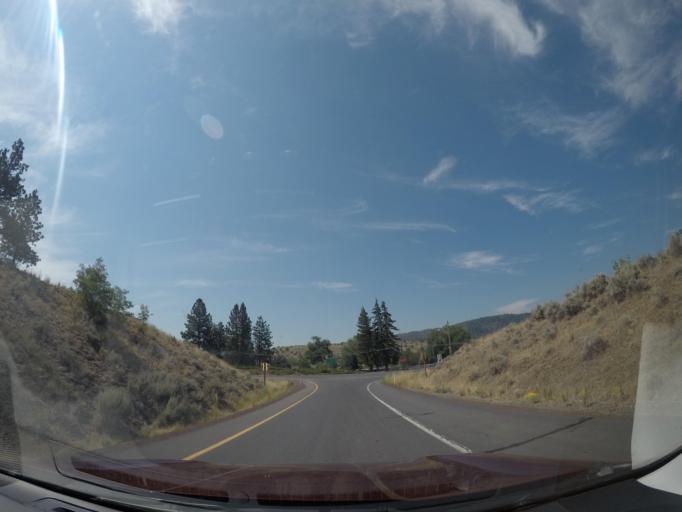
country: US
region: Oregon
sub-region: Klamath County
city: Klamath Falls
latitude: 42.2397
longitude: -121.7970
